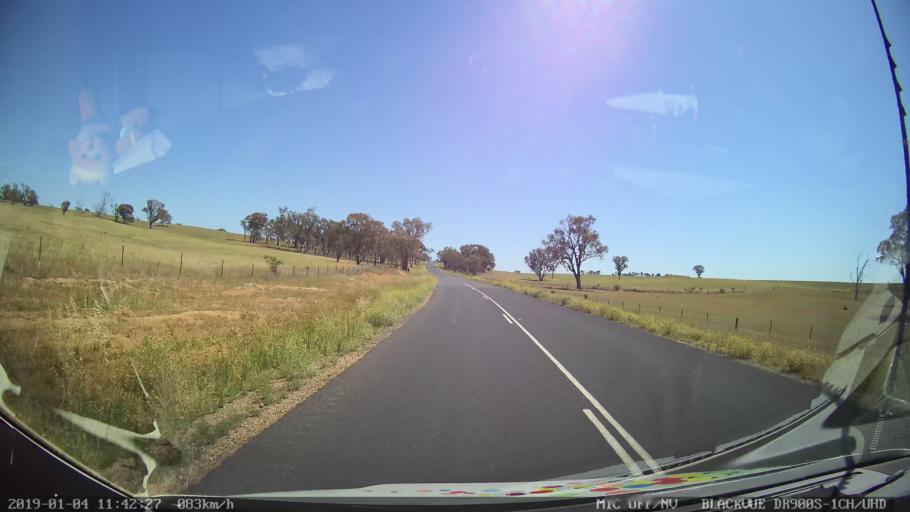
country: AU
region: New South Wales
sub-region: Cabonne
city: Molong
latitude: -32.9813
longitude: 148.7866
